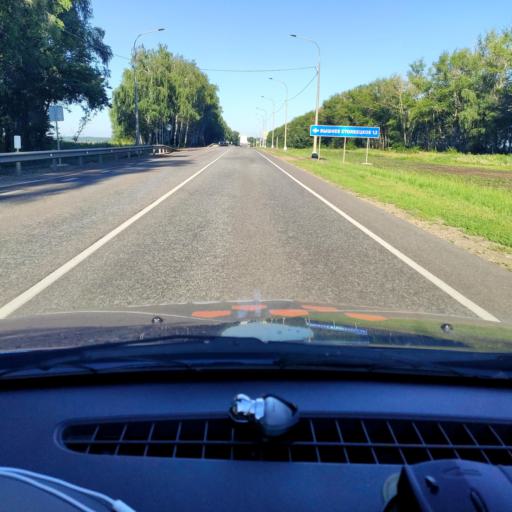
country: RU
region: Orjol
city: Pokrovskoye
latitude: 52.6375
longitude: 36.6352
